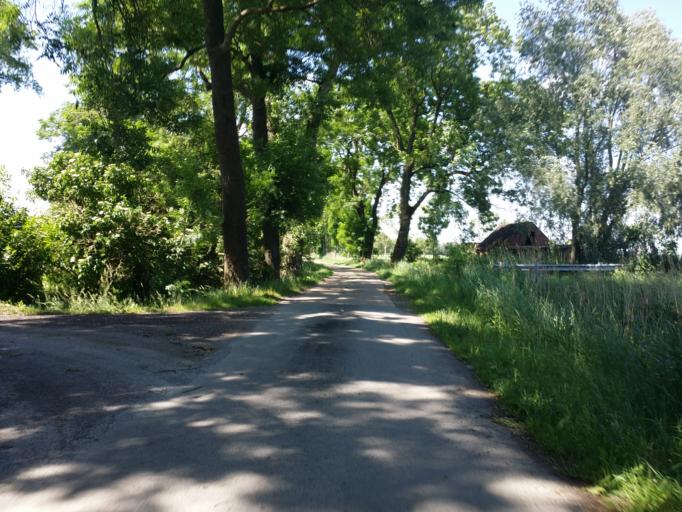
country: DE
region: Lower Saxony
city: Neuenkirchen
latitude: 53.1659
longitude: 8.5106
